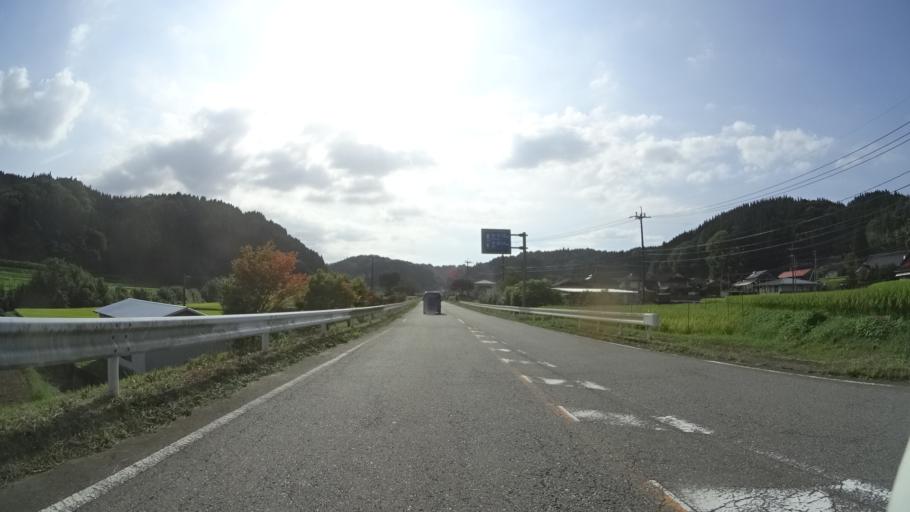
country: JP
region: Kumamoto
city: Ozu
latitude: 32.6785
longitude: 131.0372
